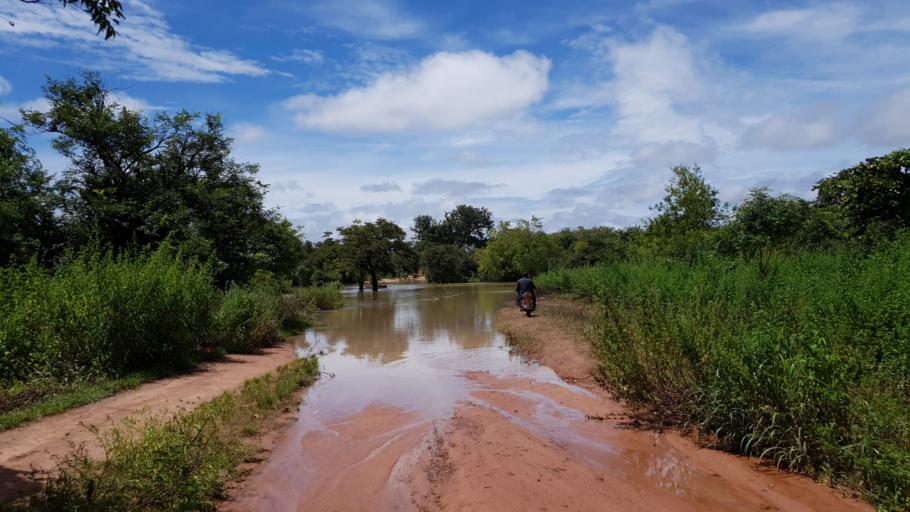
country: CI
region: Savanes
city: Tengrela
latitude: 10.3555
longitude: -6.9183
